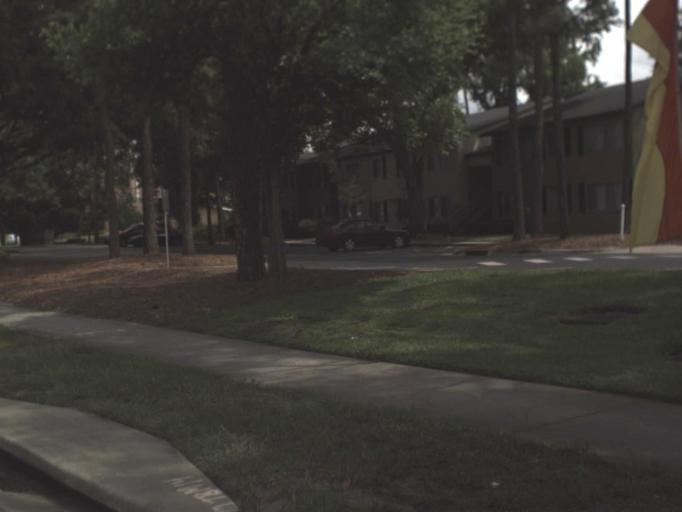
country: US
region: Florida
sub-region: Duval County
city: Jacksonville
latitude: 30.4310
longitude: -81.6734
